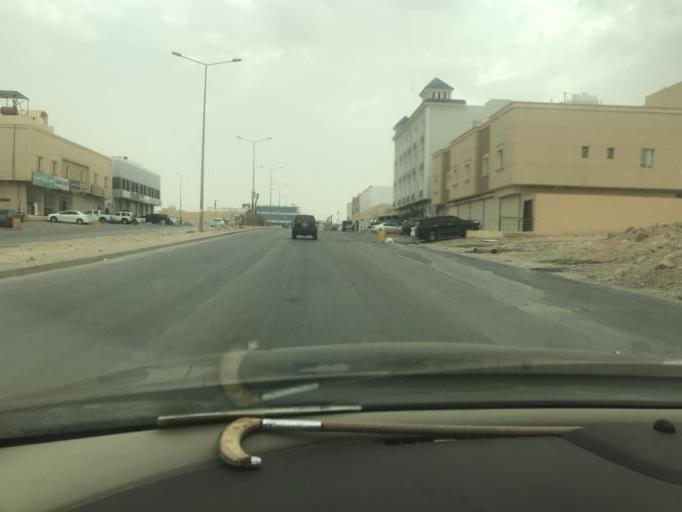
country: SA
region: Ar Riyad
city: Riyadh
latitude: 24.8113
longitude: 46.6034
